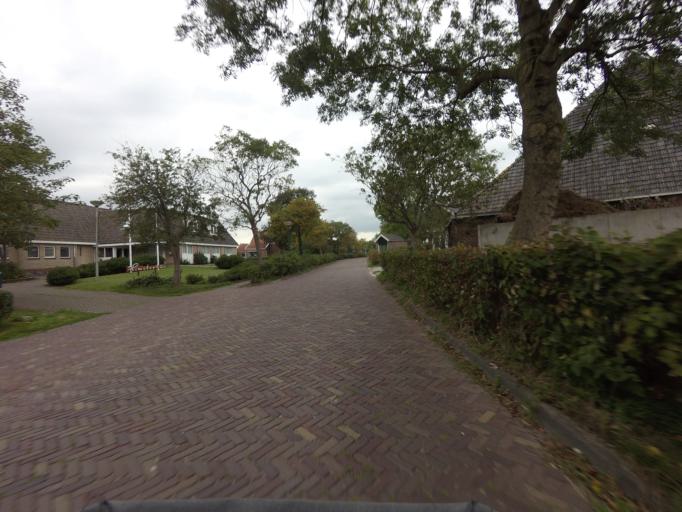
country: NL
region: Friesland
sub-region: Sudwest Fryslan
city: IJlst
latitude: 53.0156
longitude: 5.6028
